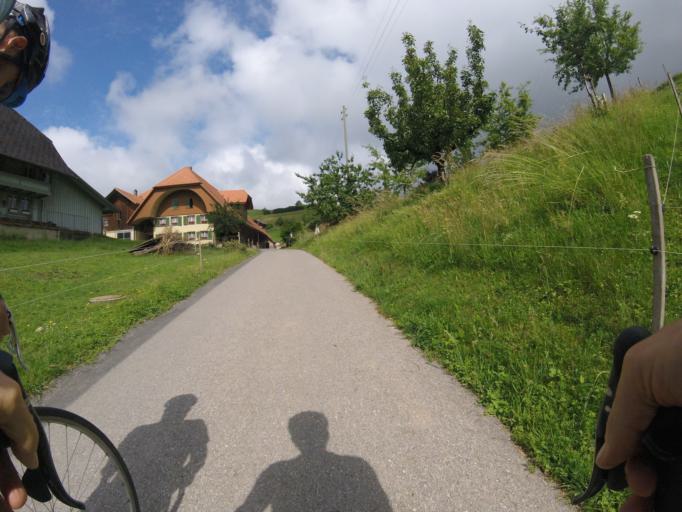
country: CH
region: Bern
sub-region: Bern-Mittelland District
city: Vechigen
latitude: 46.9744
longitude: 7.5807
